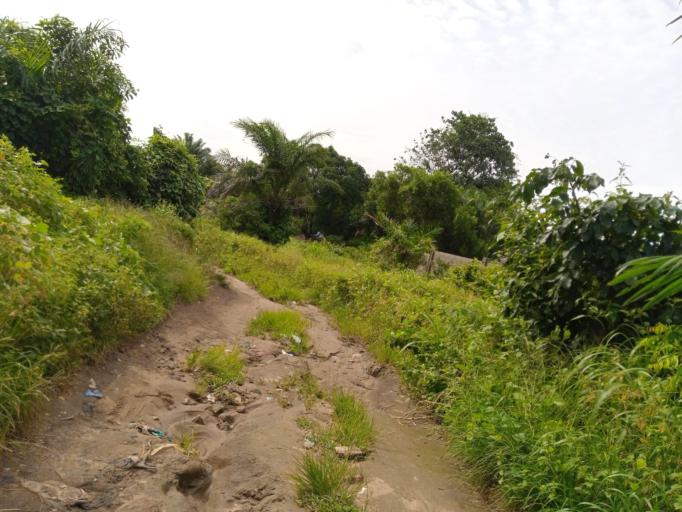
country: SL
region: Northern Province
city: Masoyila
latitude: 8.6109
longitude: -13.2016
